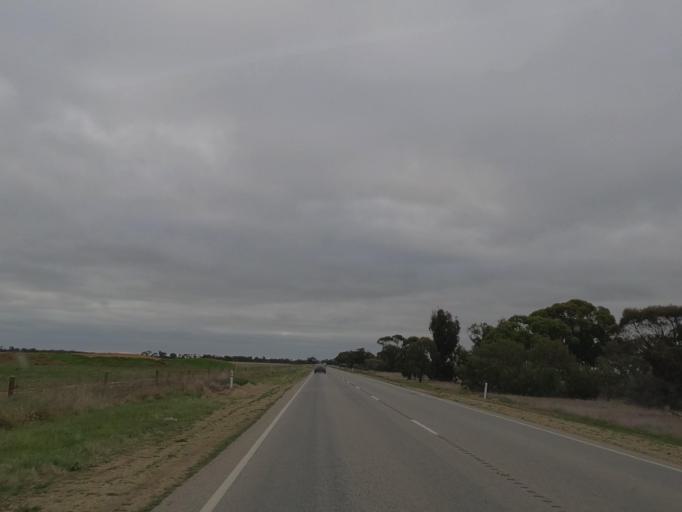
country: AU
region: Victoria
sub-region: Greater Bendigo
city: Long Gully
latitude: -36.2324
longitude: 143.9570
